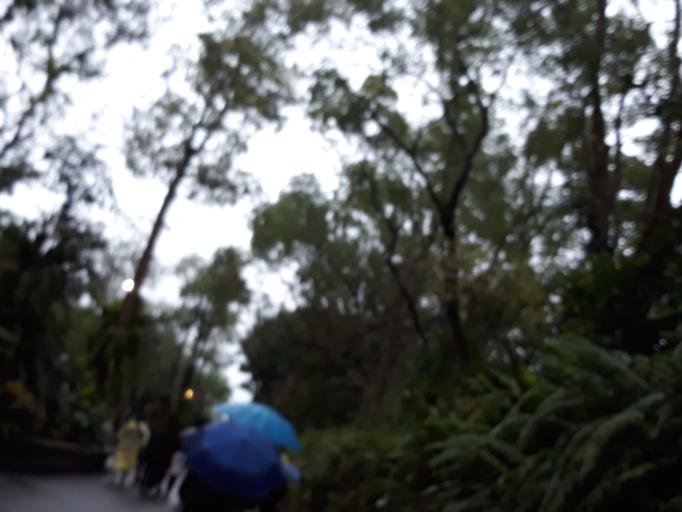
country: TW
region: Taipei
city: Taipei
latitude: 24.9974
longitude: 121.5828
